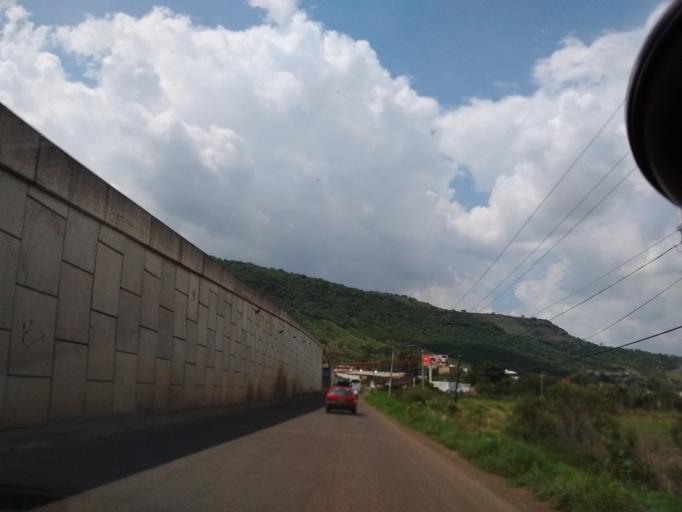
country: MX
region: Jalisco
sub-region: Atotonilco el Alto
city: Vistas del Maguey [Fraccionamiento]
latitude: 20.5362
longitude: -102.5186
